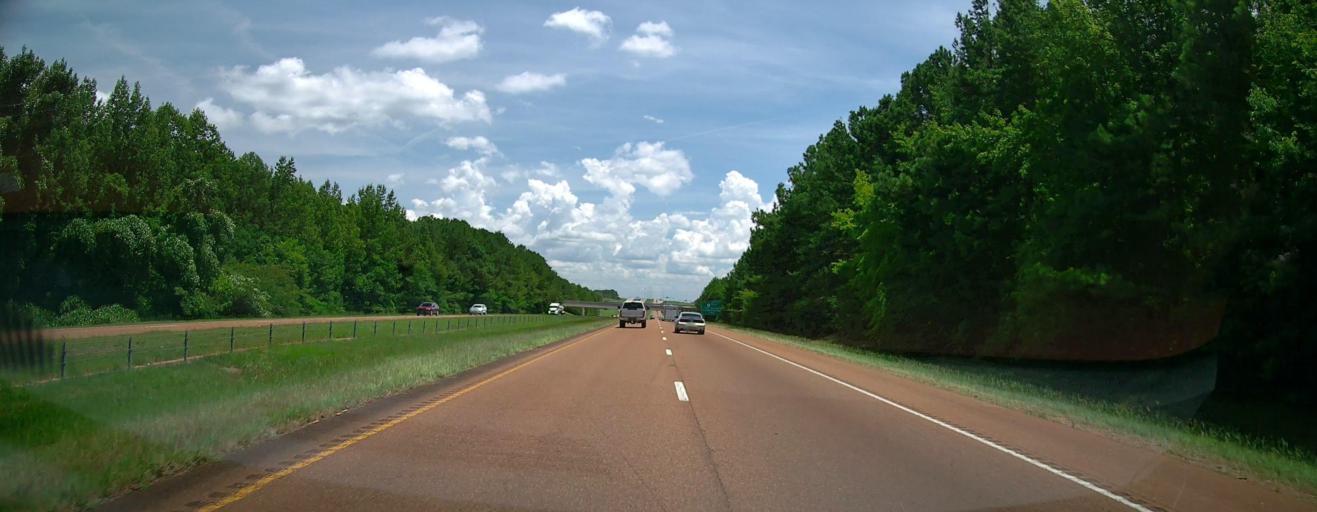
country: US
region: Mississippi
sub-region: Union County
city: New Albany
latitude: 34.4007
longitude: -88.9101
